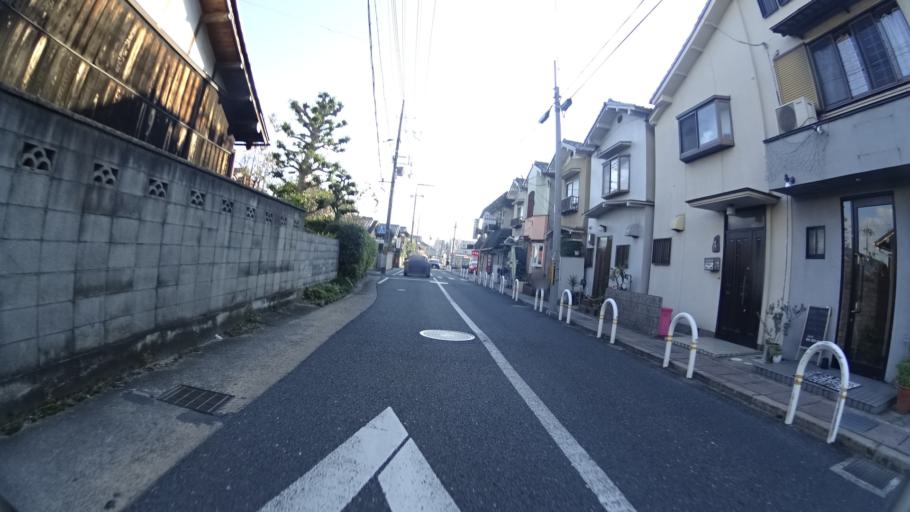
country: JP
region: Kyoto
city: Muko
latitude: 34.9552
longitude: 135.7004
